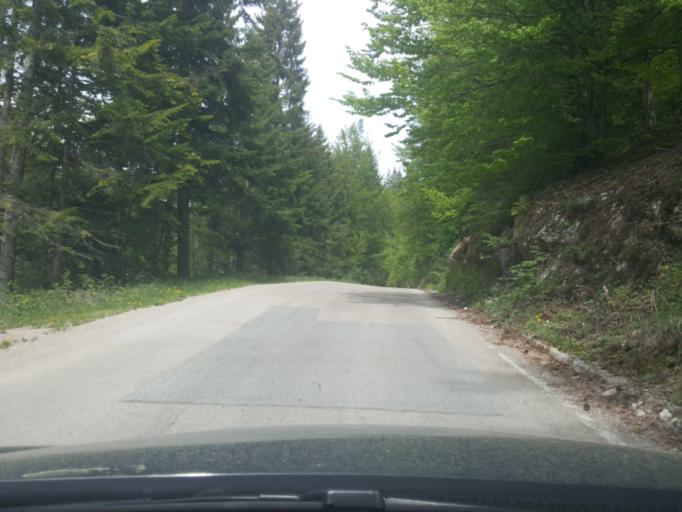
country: RS
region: Central Serbia
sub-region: Zlatiborski Okrug
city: Bajina Basta
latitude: 43.8882
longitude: 19.5248
